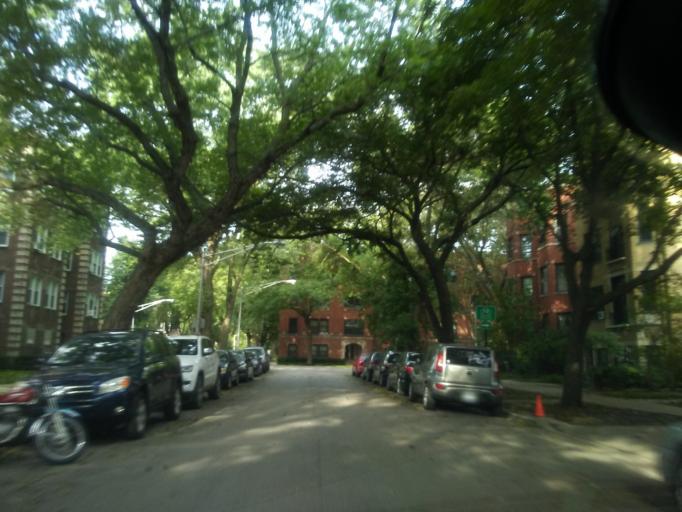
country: US
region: Illinois
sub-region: Cook County
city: Evanston
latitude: 41.9746
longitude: -87.6640
